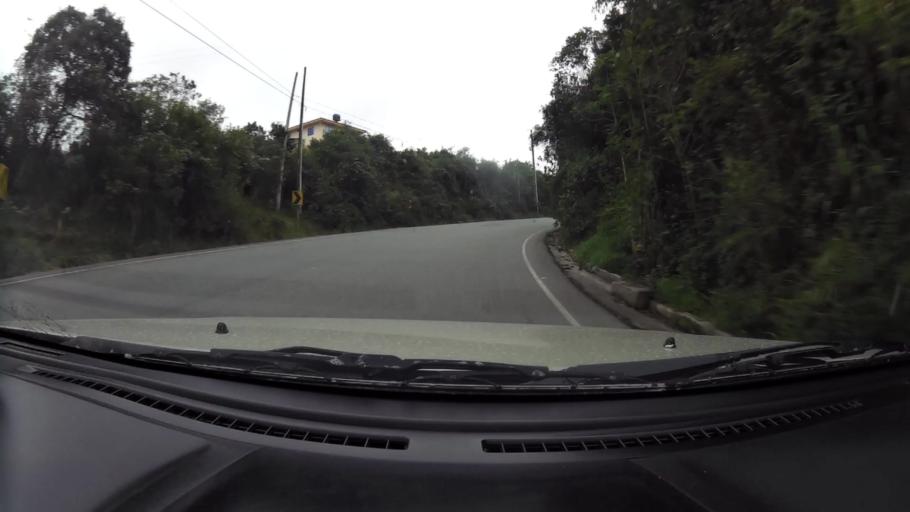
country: EC
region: Canar
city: Canar
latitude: -2.3929
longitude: -78.9873
